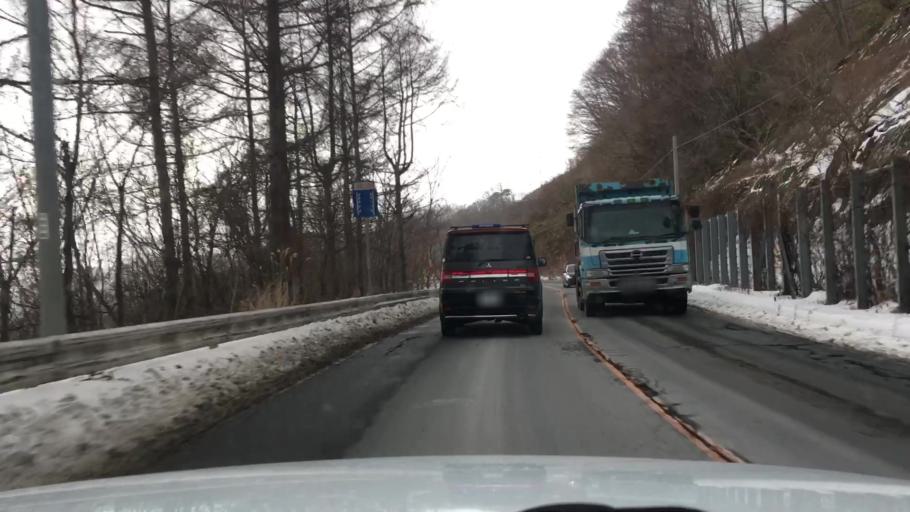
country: JP
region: Iwate
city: Morioka-shi
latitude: 39.6580
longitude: 141.3387
